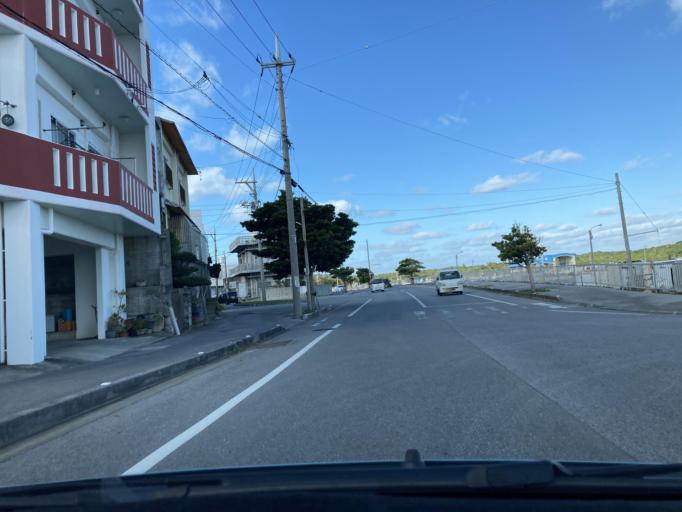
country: JP
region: Okinawa
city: Katsuren-haebaru
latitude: 26.3085
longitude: 127.9204
